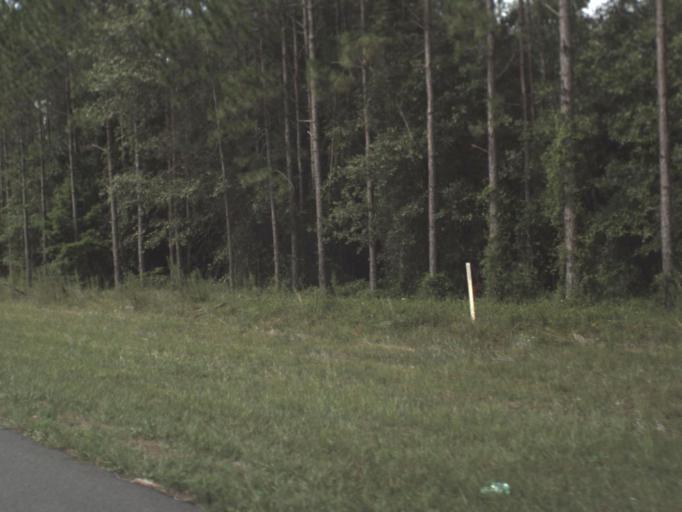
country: US
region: Florida
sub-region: Columbia County
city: Five Points
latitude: 30.4057
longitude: -82.6337
